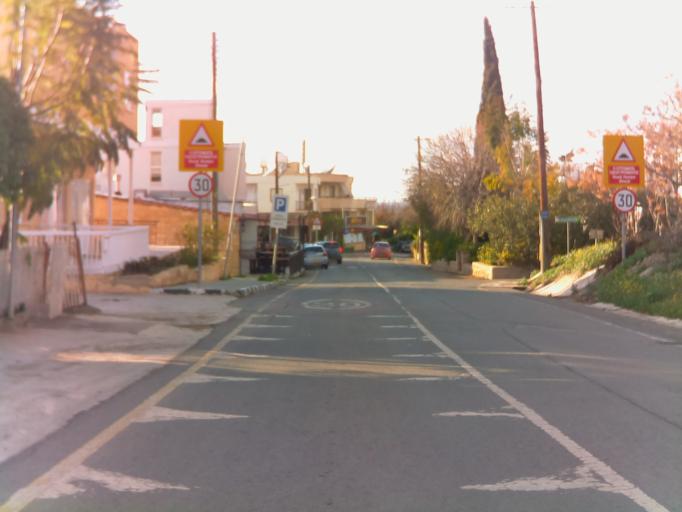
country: CY
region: Pafos
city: Kissonerga
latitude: 34.8222
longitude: 32.4037
